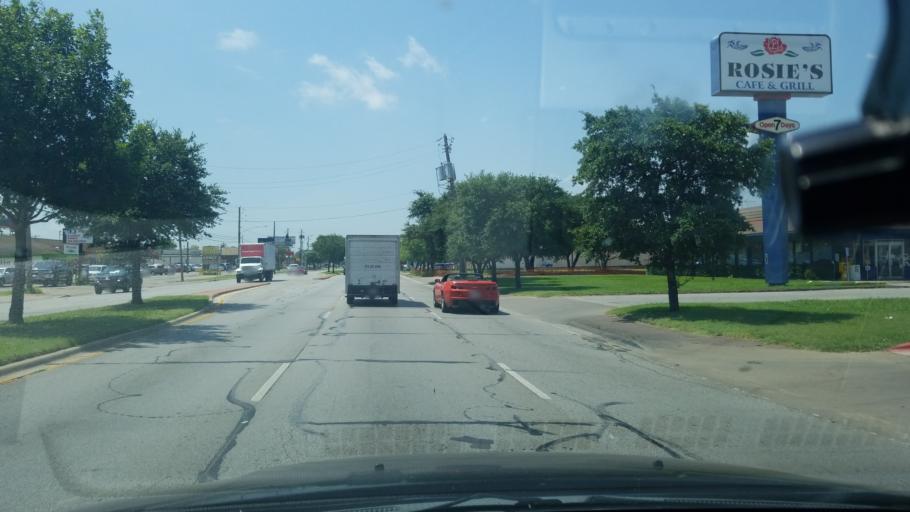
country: US
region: Texas
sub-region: Dallas County
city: Balch Springs
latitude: 32.7410
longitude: -96.6830
